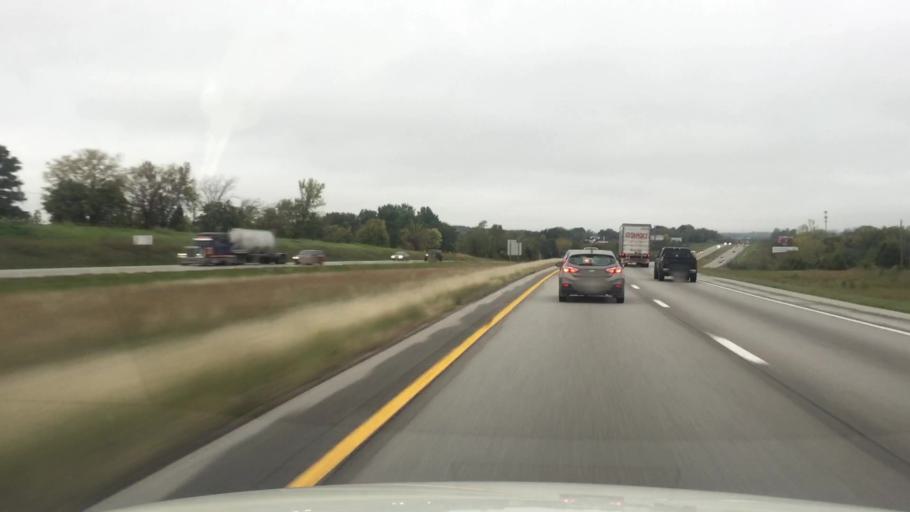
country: US
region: Missouri
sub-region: Jackson County
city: Oak Grove
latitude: 39.0170
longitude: -94.1551
